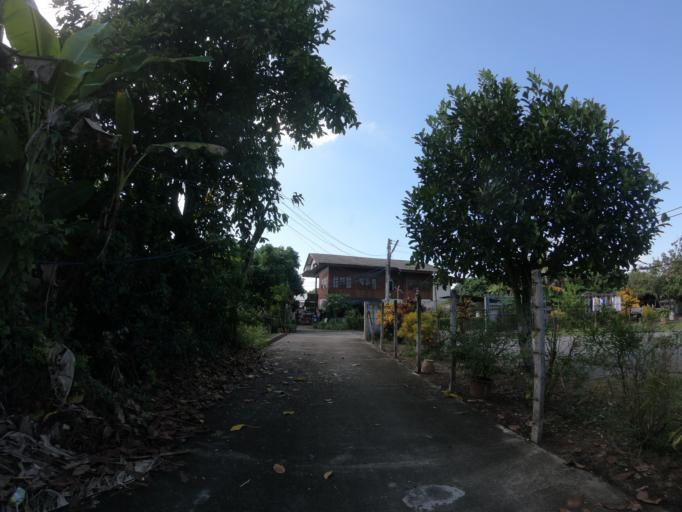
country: TH
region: Chiang Mai
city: Saraphi
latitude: 18.7064
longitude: 99.0042
